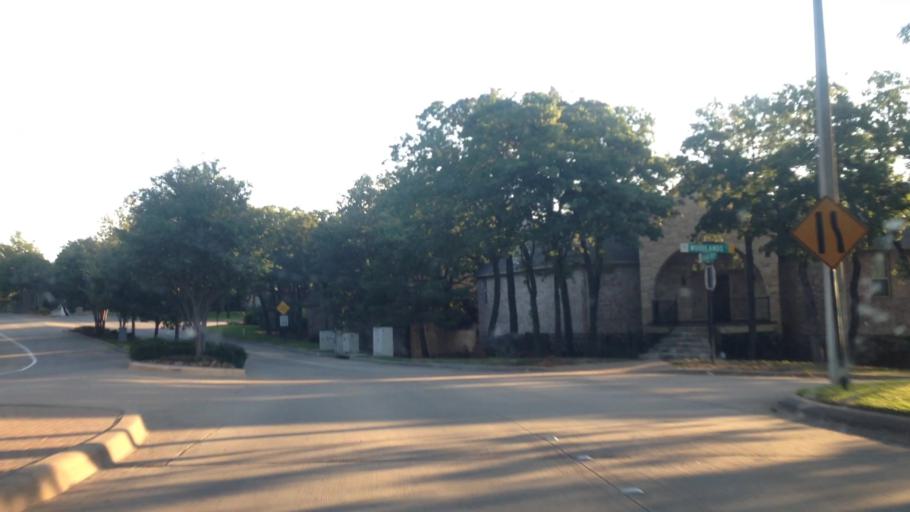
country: US
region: Texas
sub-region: Denton County
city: Trophy Club
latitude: 32.9919
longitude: -97.1688
